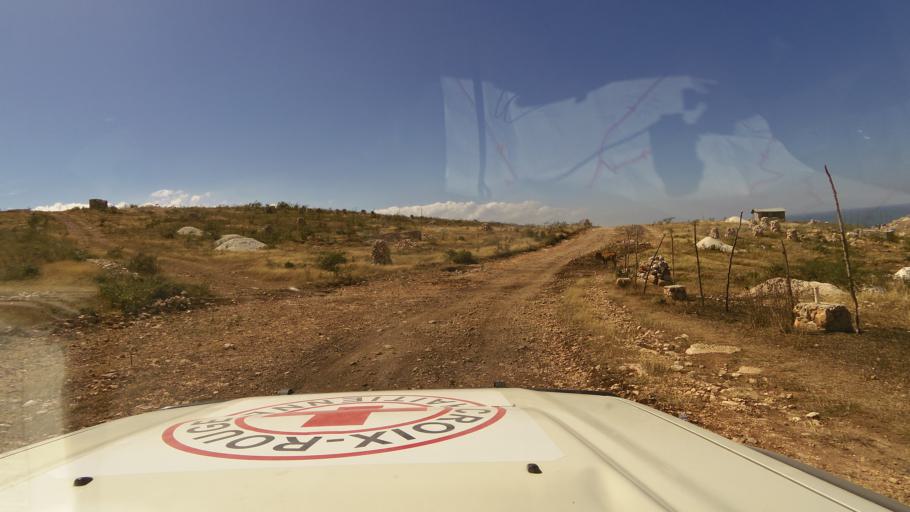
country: HT
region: Ouest
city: Croix des Bouquets
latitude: 18.6752
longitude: -72.2945
